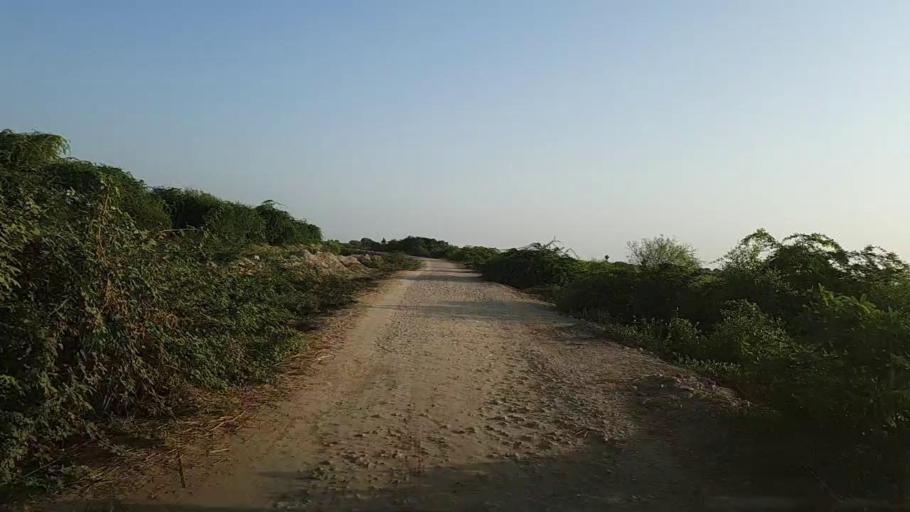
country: PK
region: Sindh
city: Kario
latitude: 24.7093
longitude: 68.6667
